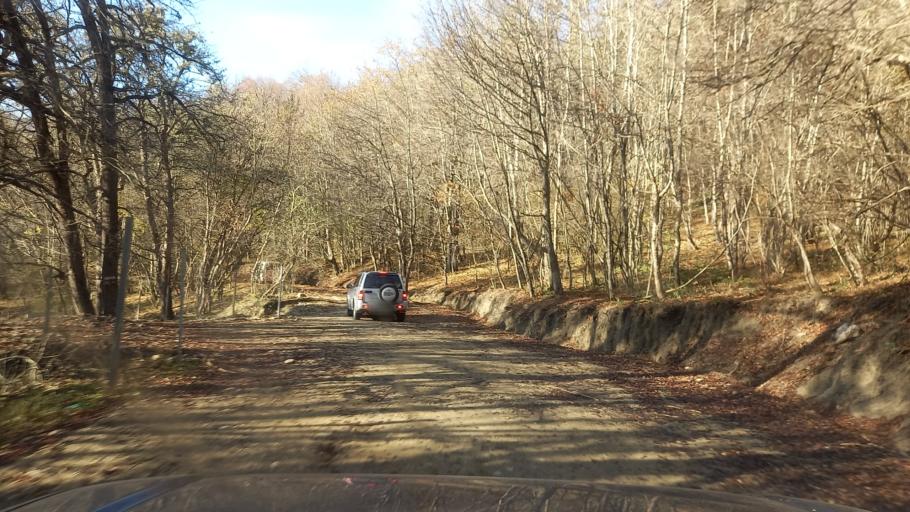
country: RU
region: Adygeya
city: Kamennomostskiy
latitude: 44.1140
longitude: 40.1176
